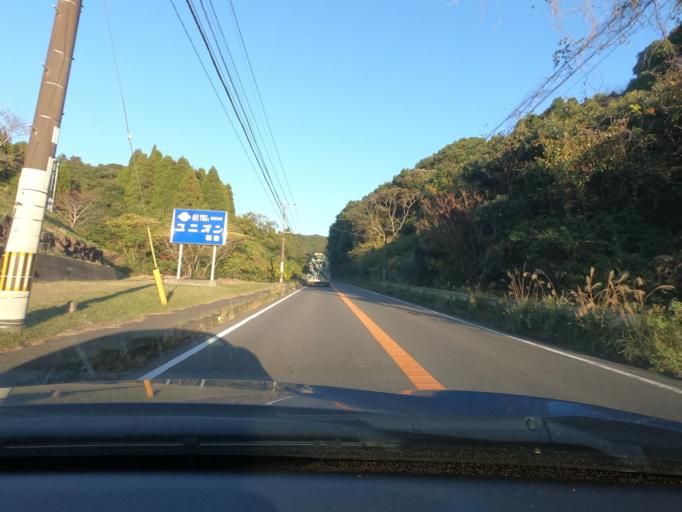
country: JP
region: Kagoshima
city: Satsumasendai
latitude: 31.8059
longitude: 130.3644
